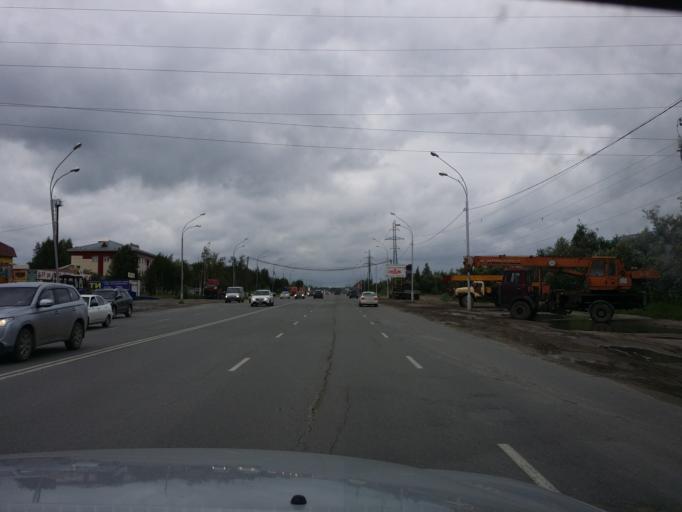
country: RU
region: Khanty-Mansiyskiy Avtonomnyy Okrug
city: Nizhnevartovsk
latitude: 60.9525
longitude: 76.5301
